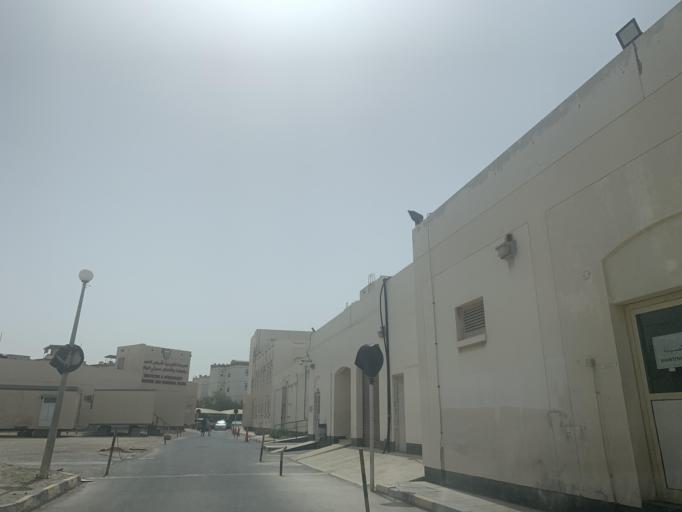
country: BH
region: Manama
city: Jidd Hafs
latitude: 26.2176
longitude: 50.5403
